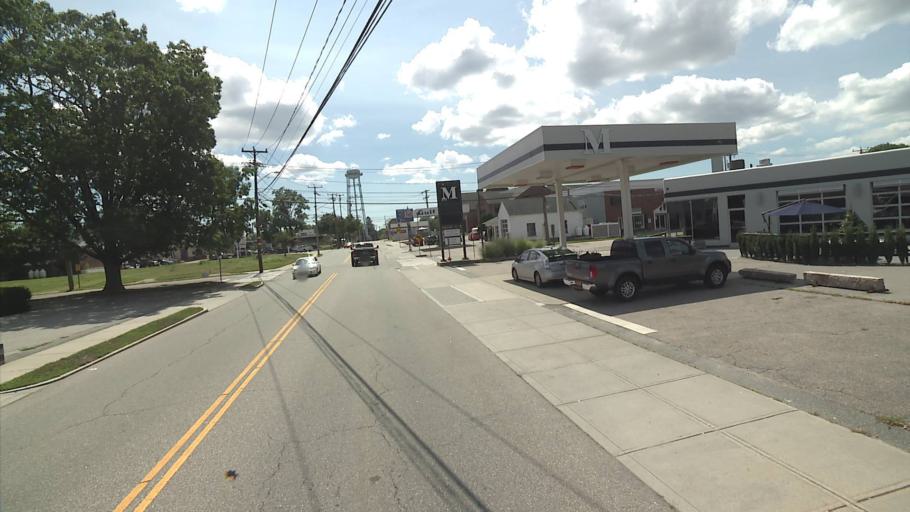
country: US
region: Connecticut
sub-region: New London County
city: Mystic
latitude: 41.3522
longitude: -71.9639
